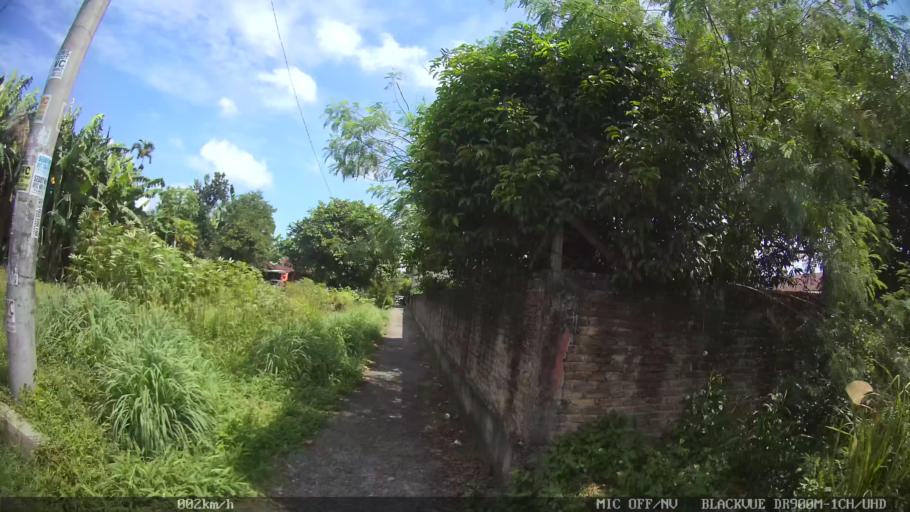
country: ID
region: North Sumatra
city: Medan
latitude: 3.6022
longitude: 98.7527
